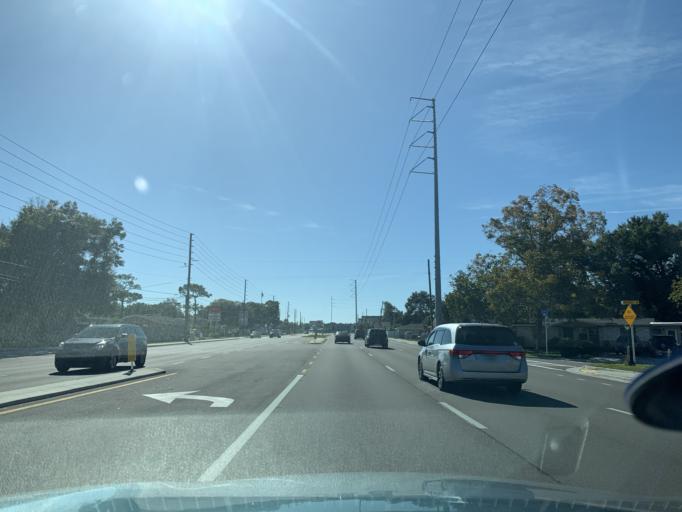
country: US
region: Florida
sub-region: Pinellas County
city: Seminole
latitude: 27.8441
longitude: -82.7624
